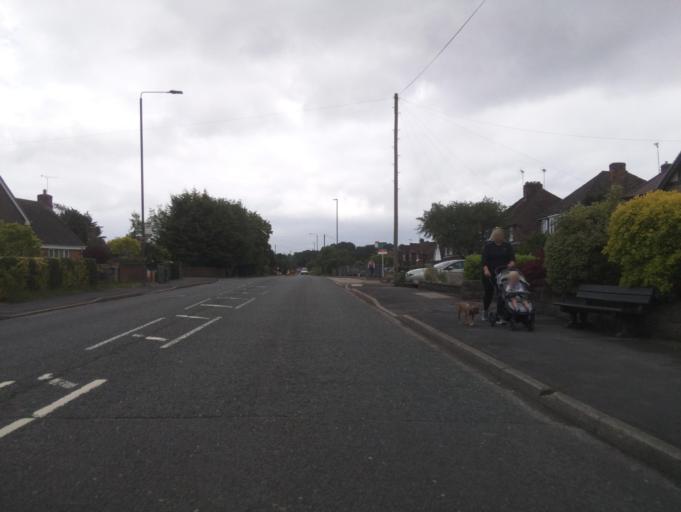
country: GB
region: England
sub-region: Derbyshire
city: Ashbourne
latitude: 53.0099
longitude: -1.7217
